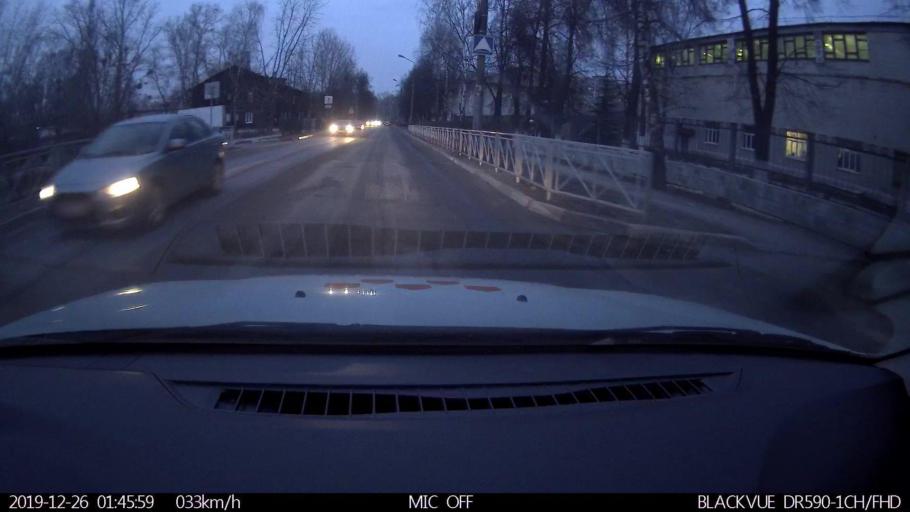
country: RU
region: Nizjnij Novgorod
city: Nizhniy Novgorod
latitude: 56.3240
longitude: 43.8685
